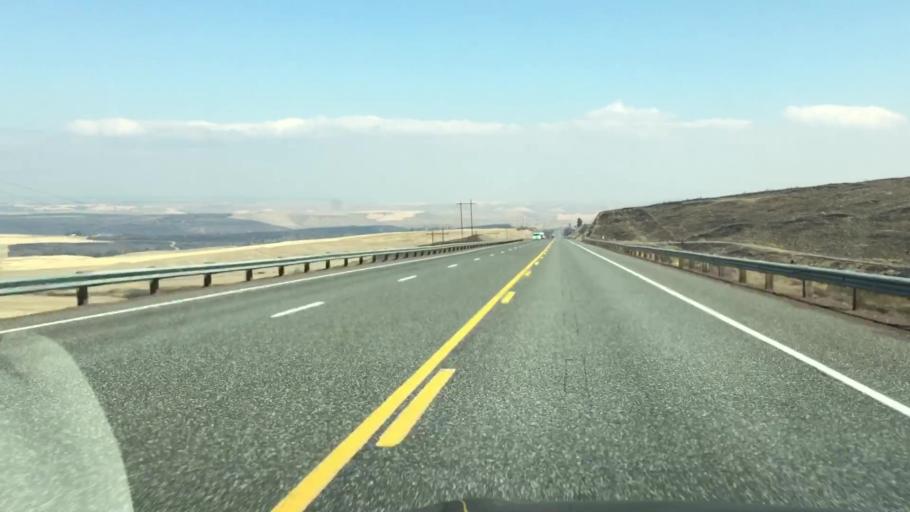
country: US
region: Oregon
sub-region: Wasco County
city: The Dalles
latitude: 45.3670
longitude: -121.1408
